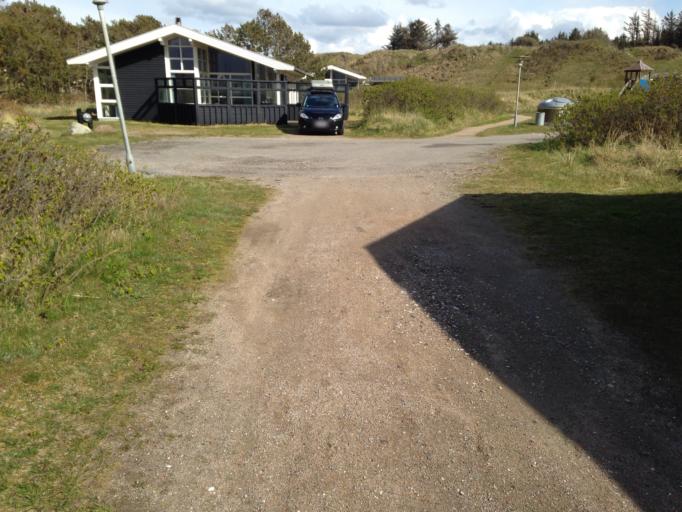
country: DK
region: North Denmark
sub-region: Hjorring Kommune
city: Hjorring
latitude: 57.4906
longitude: 9.8360
